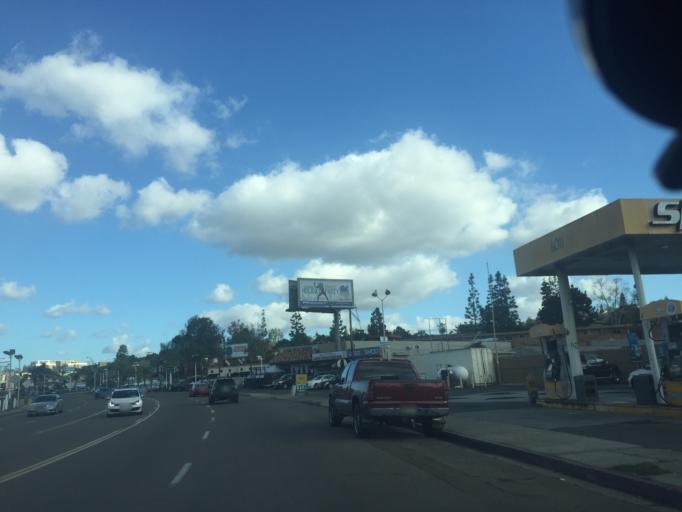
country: US
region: California
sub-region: San Diego County
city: La Mesa
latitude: 32.7832
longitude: -117.0983
